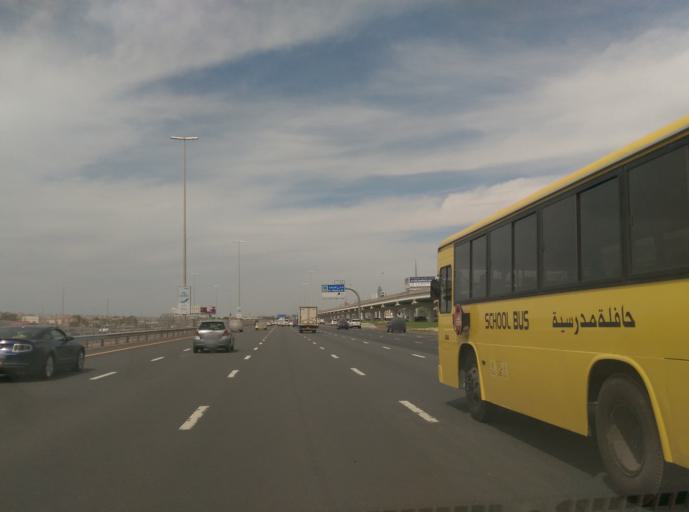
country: AE
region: Dubai
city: Dubai
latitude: 25.1402
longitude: 55.2183
